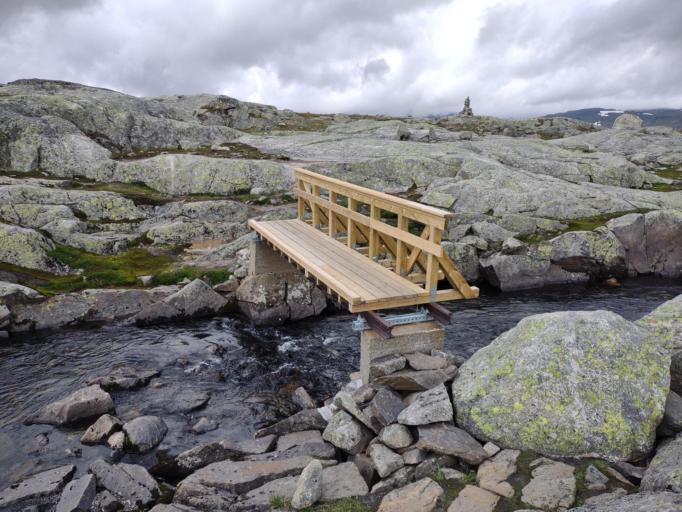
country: NO
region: Hordaland
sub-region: Eidfjord
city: Eidfjord
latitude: 60.5607
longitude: 7.5339
